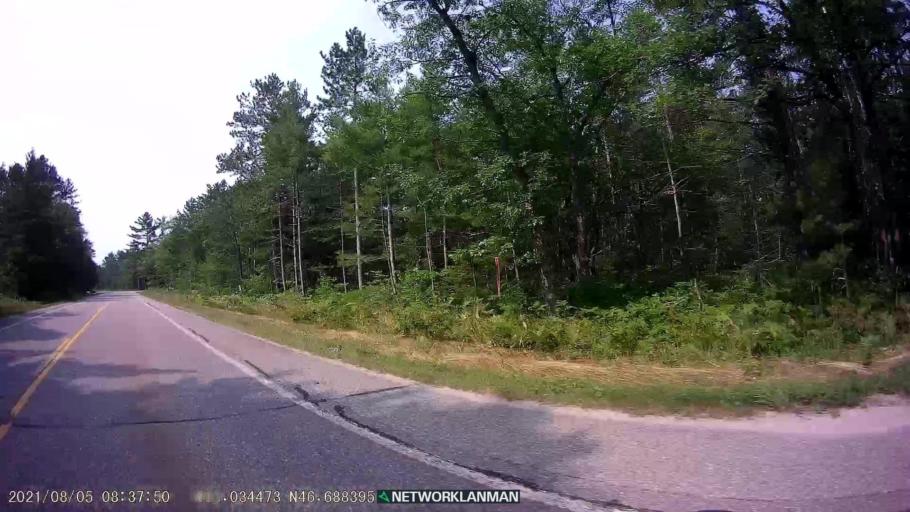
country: US
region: Michigan
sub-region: Luce County
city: Newberry
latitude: 46.6879
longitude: -85.0346
